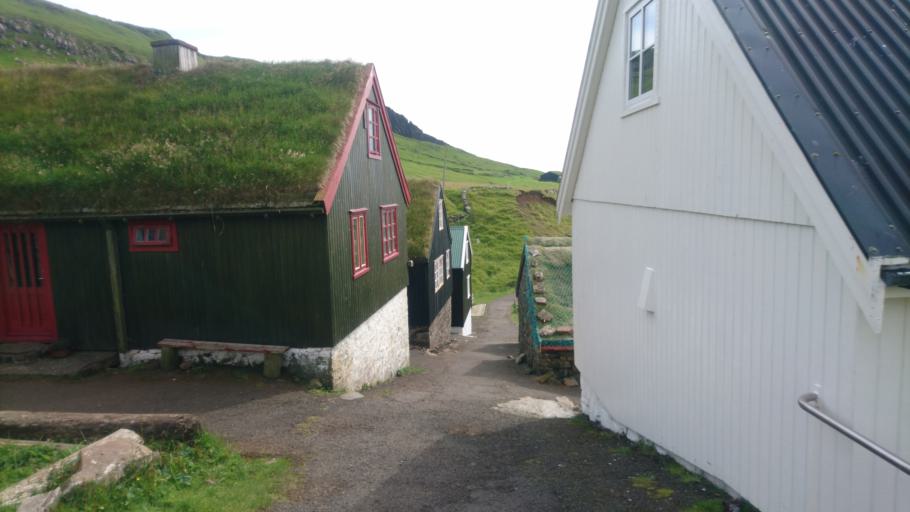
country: FO
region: Vagar
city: Sorvagur
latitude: 62.1037
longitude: -7.6442
